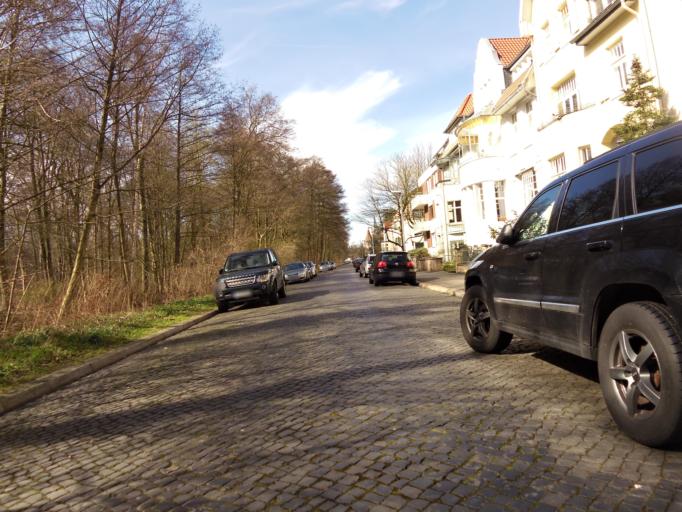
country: DE
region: Lower Saxony
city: Laatzen
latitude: 52.3697
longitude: 9.7901
